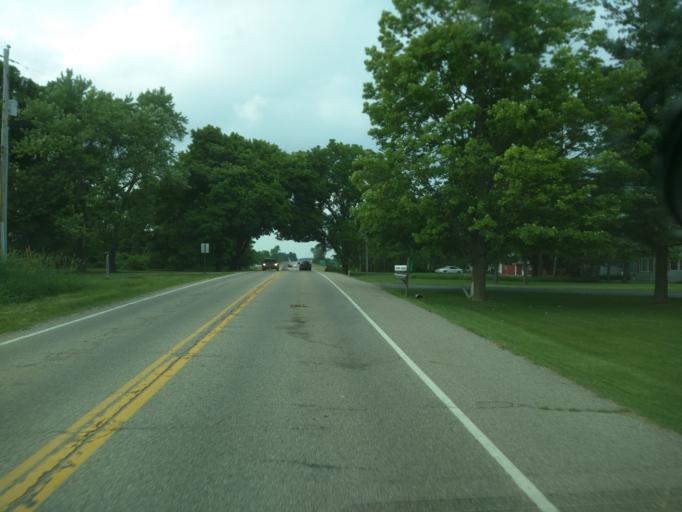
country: US
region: Michigan
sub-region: Clinton County
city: DeWitt
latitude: 42.8028
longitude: -84.6027
